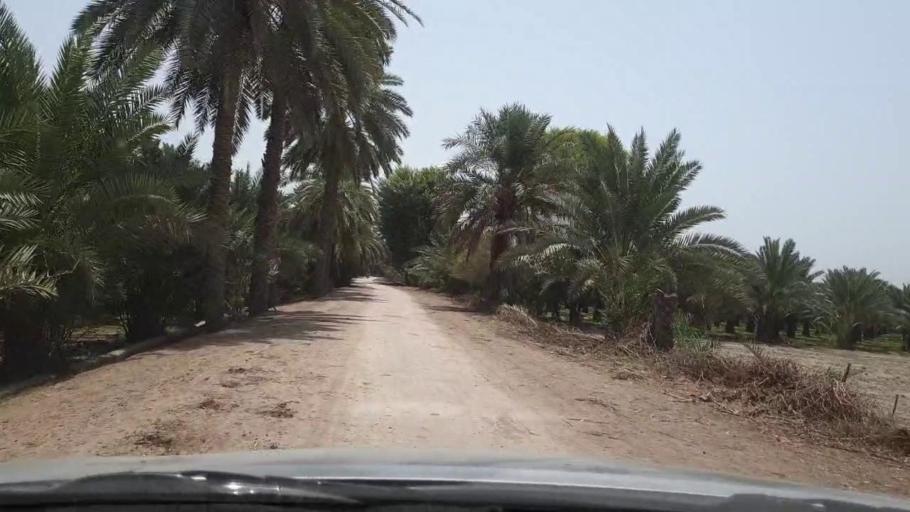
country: PK
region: Sindh
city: Pano Aqil
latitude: 27.8615
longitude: 69.0660
